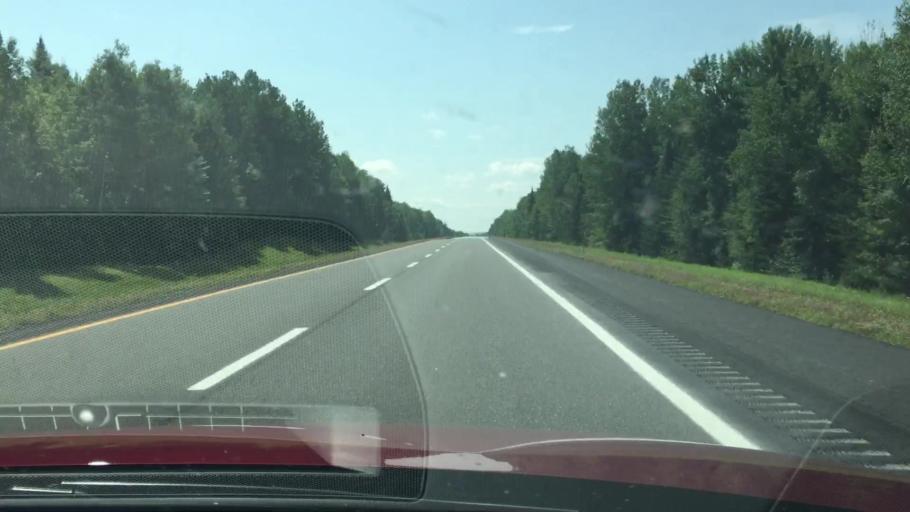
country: US
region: Maine
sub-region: Penobscot County
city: Patten
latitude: 45.9461
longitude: -68.3407
